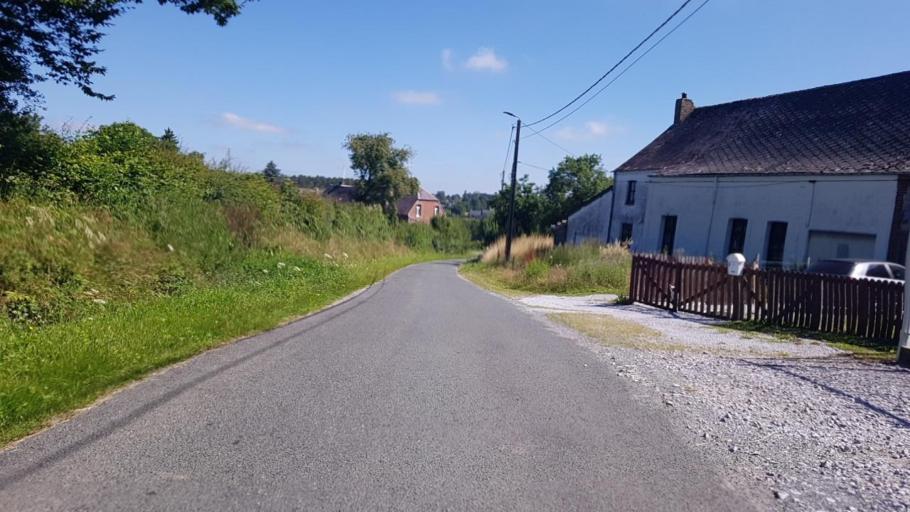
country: BE
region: Wallonia
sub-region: Province du Hainaut
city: Momignies
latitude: 50.0129
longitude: 4.1505
